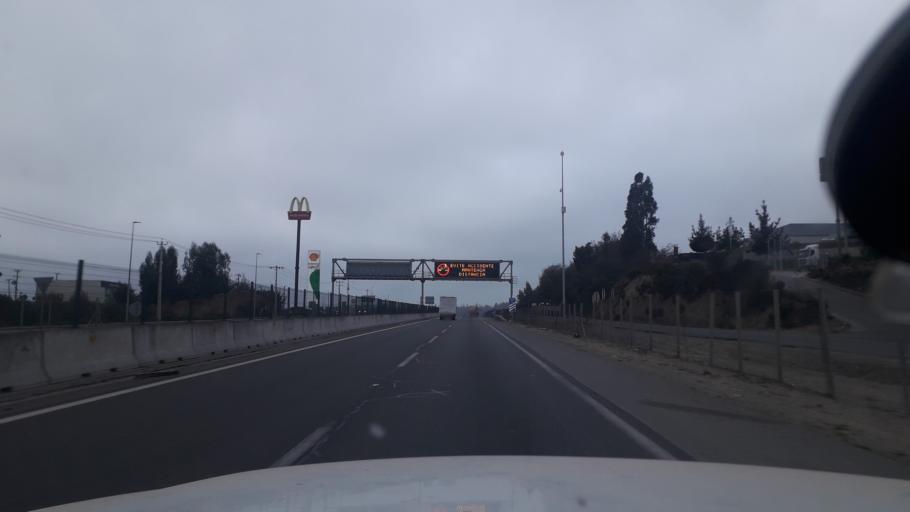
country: CL
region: Valparaiso
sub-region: Provincia de Valparaiso
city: Vina del Mar
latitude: -33.1238
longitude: -71.5612
